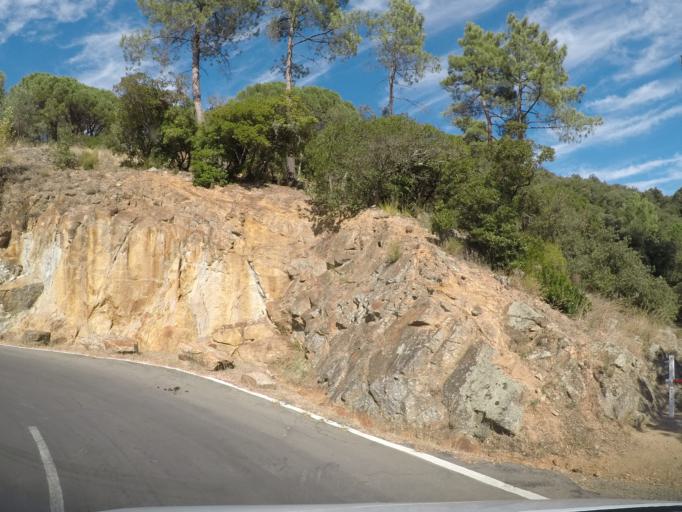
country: FR
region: Languedoc-Roussillon
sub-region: Departement du Gard
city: Anduze
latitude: 44.0759
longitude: 3.9642
